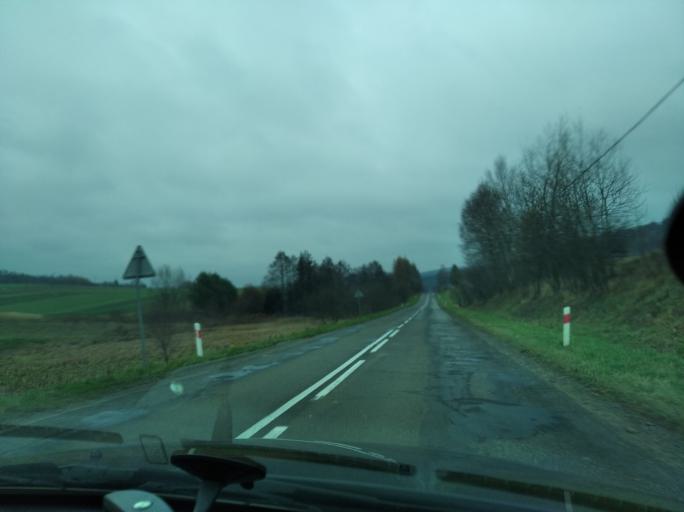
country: PL
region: Subcarpathian Voivodeship
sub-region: Powiat rzeszowski
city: Dynow
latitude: 49.8477
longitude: 22.2448
